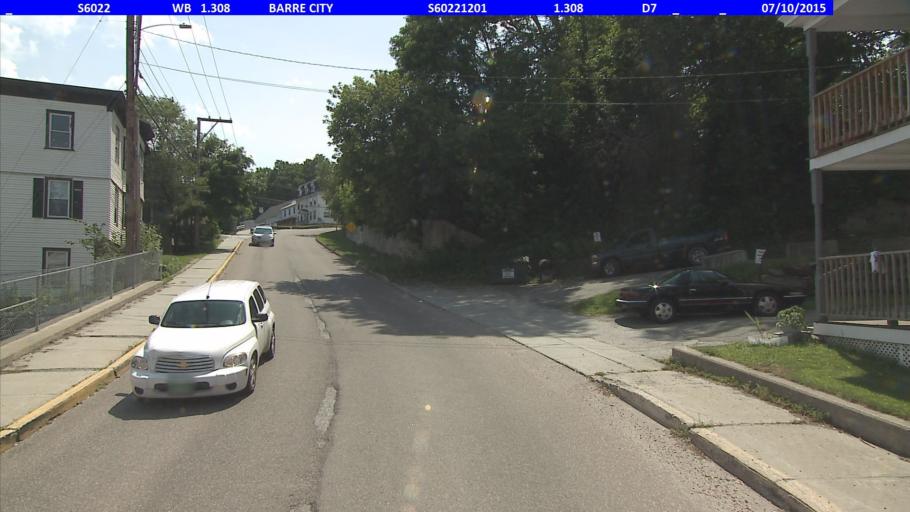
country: US
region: Vermont
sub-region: Washington County
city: Barre
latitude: 44.1963
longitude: -72.5040
